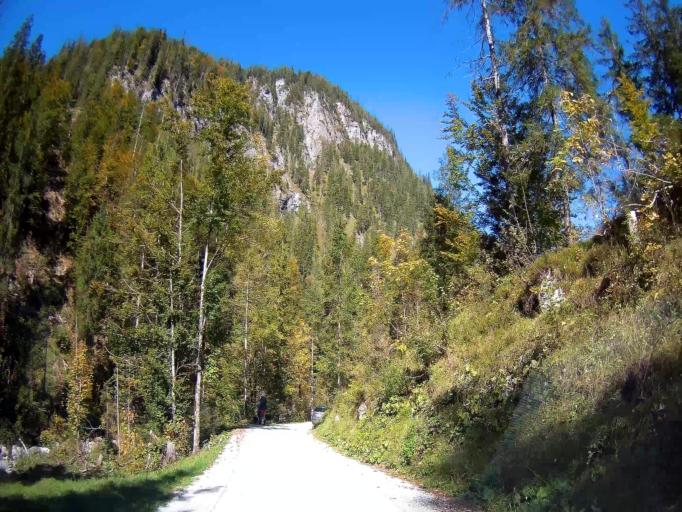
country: AT
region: Salzburg
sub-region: Politischer Bezirk Zell am See
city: Sankt Martin bei Lofer
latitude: 47.5213
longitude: 12.7070
